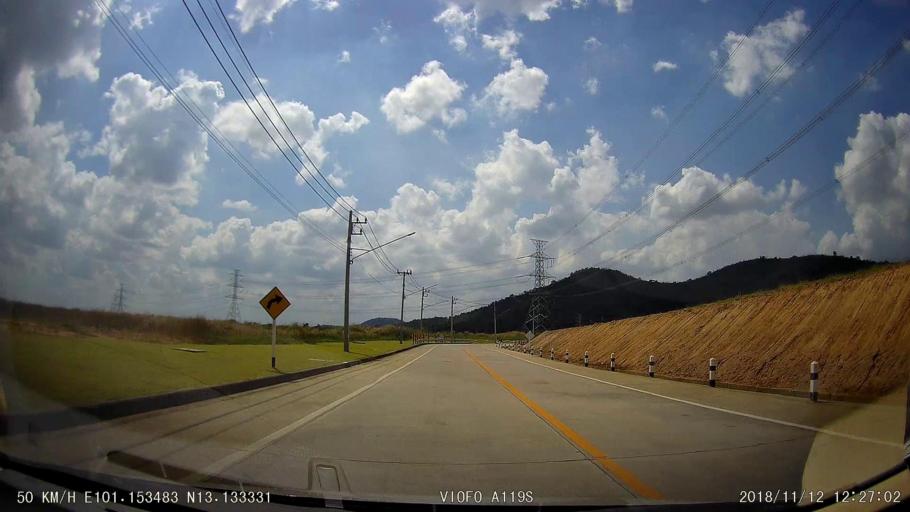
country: TH
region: Chon Buri
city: Ban Talat Bueng
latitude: 13.1331
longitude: 101.1532
